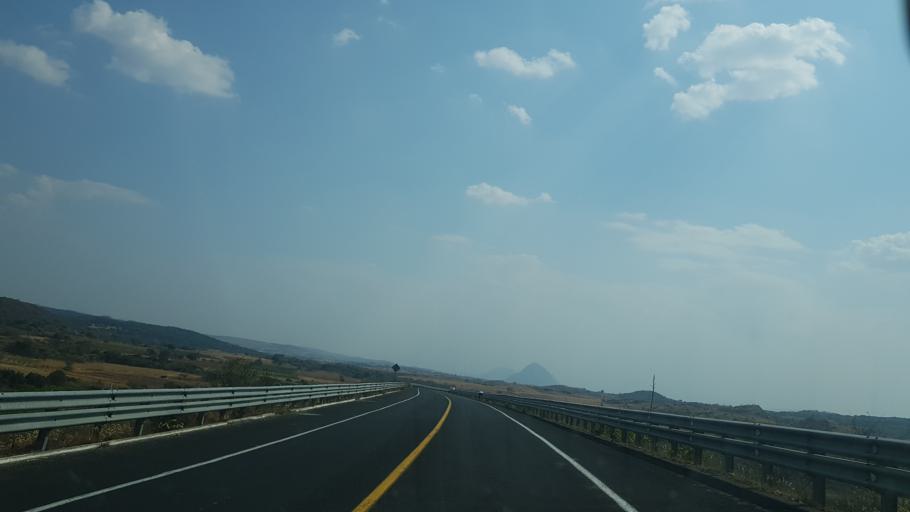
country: MX
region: Puebla
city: San Juan Amecac
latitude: 18.8172
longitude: -98.6951
